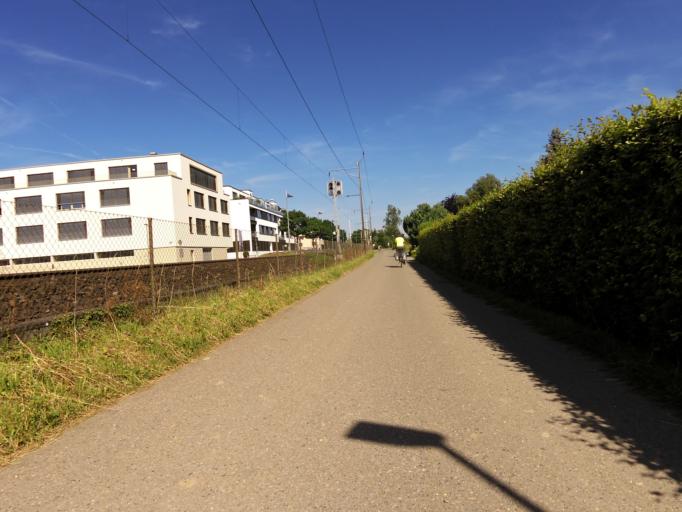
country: CH
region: Thurgau
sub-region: Kreuzlingen District
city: Bottighofen
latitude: 47.6401
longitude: 9.2145
